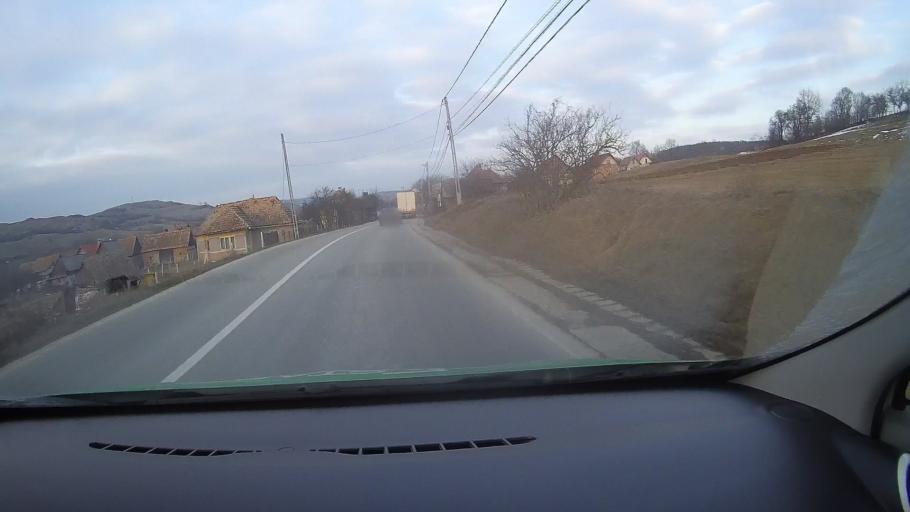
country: RO
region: Harghita
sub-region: Comuna Simonesti
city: Simonesti
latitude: 46.3393
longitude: 25.1118
